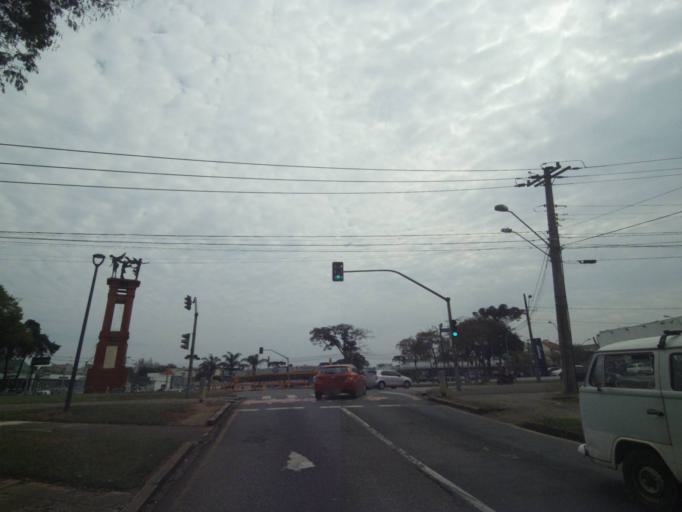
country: BR
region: Parana
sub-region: Curitiba
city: Curitiba
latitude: -25.4526
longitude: -49.3043
